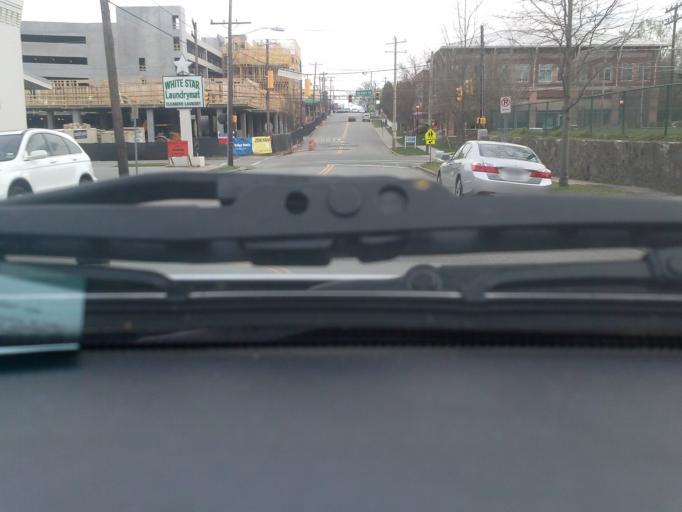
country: US
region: North Carolina
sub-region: Durham County
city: Durham
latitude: 36.0123
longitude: -78.9219
